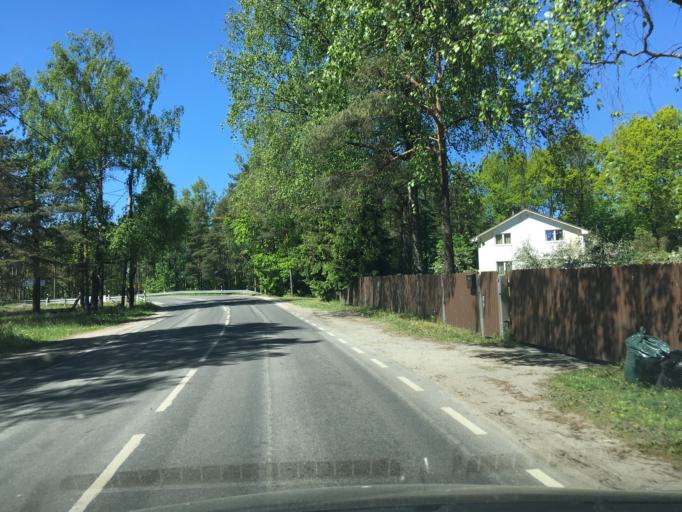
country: EE
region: Harju
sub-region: Saue vald
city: Laagri
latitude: 59.3867
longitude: 24.6465
